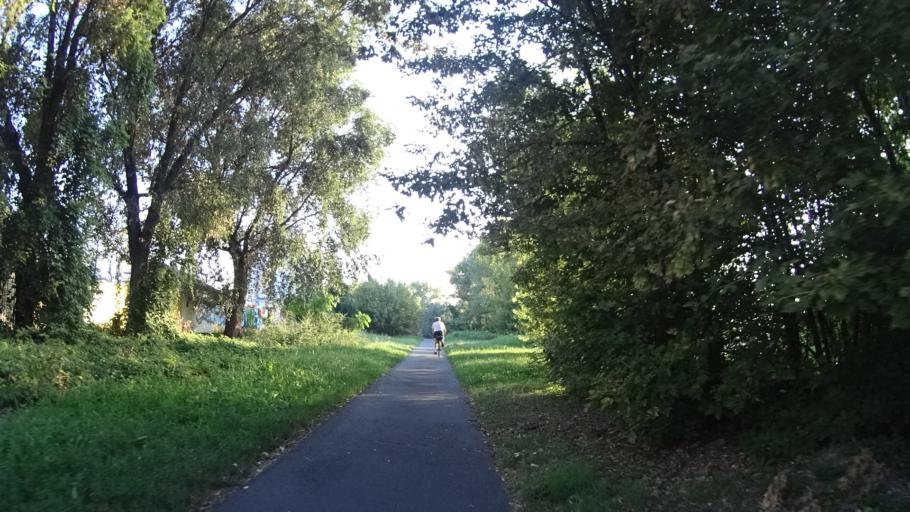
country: HU
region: Budapest
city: Budapest XXII. keruelet
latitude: 47.4096
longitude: 19.0394
